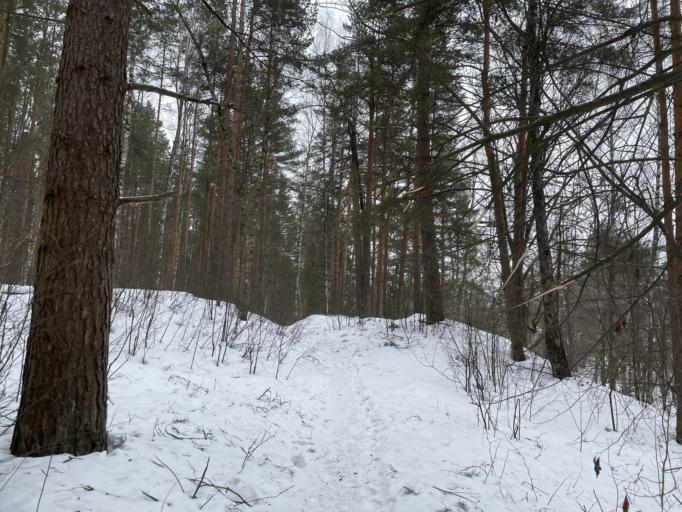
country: RU
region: Vladimir
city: Pokrov
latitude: 55.9395
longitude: 39.2372
